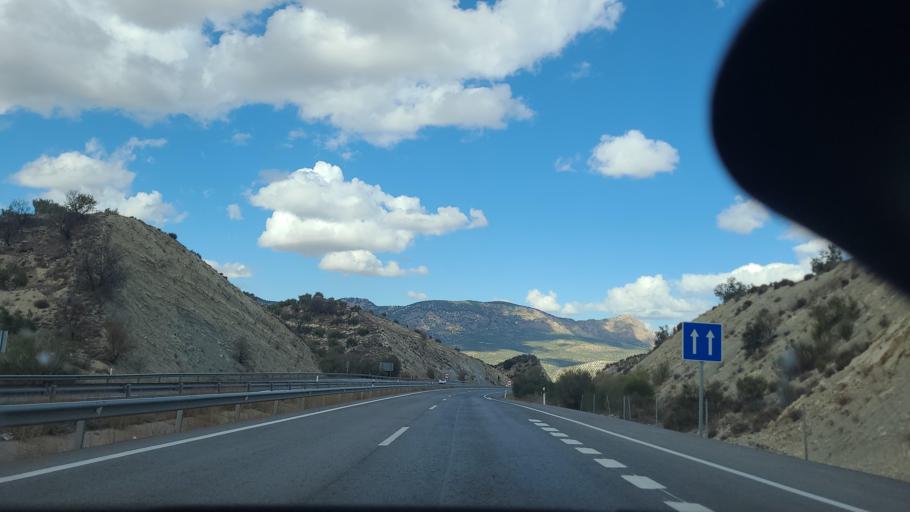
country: ES
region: Andalusia
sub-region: Provincia de Jaen
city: Campillo de Arenas
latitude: 37.5372
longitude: -3.6358
